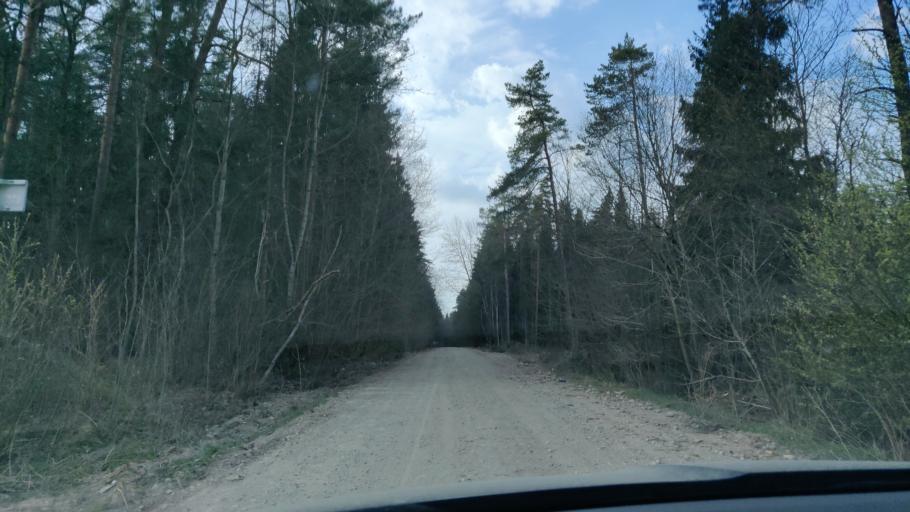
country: LT
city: Lentvaris
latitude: 54.5977
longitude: 25.0806
